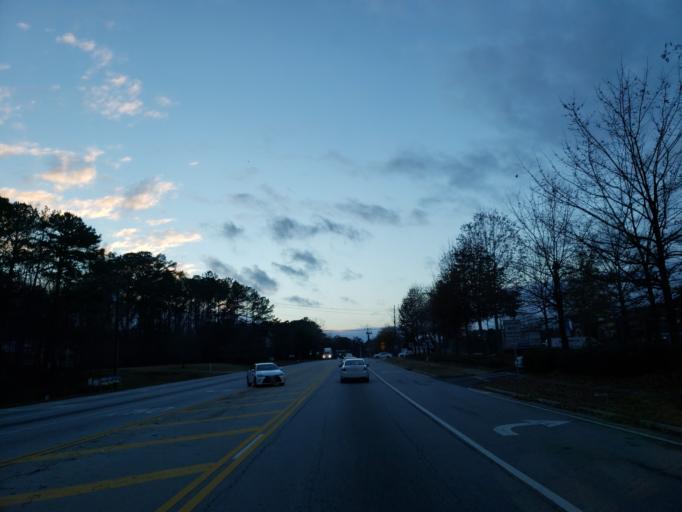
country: US
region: Georgia
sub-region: Fulton County
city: Union City
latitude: 33.6993
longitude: -84.5774
